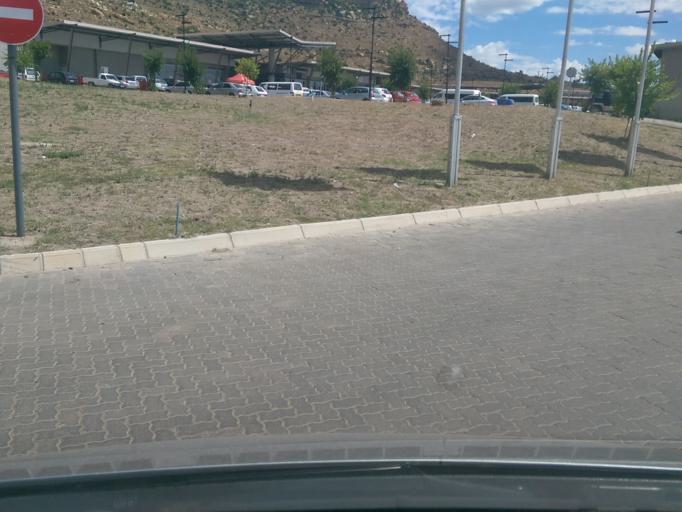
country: LS
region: Maseru
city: Maseru
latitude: -29.3347
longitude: 27.4857
